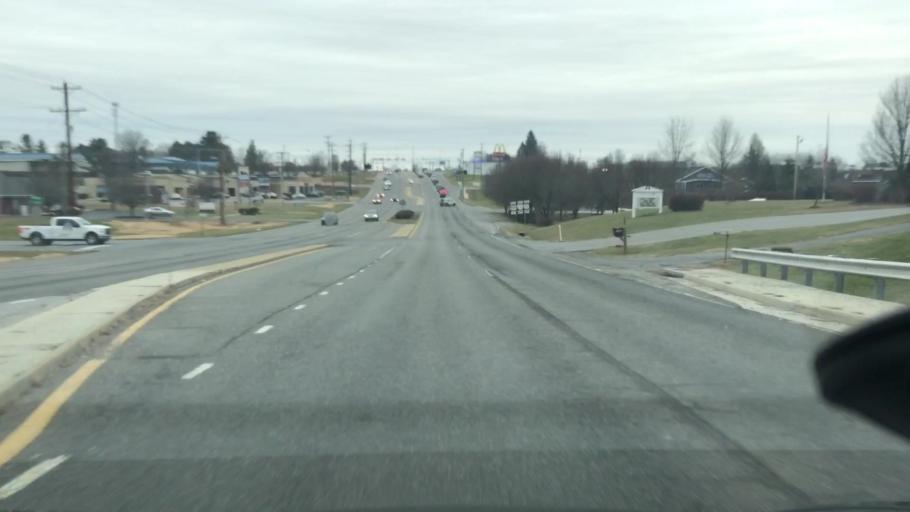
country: US
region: Virginia
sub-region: Montgomery County
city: Christiansburg
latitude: 37.1482
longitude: -80.4148
